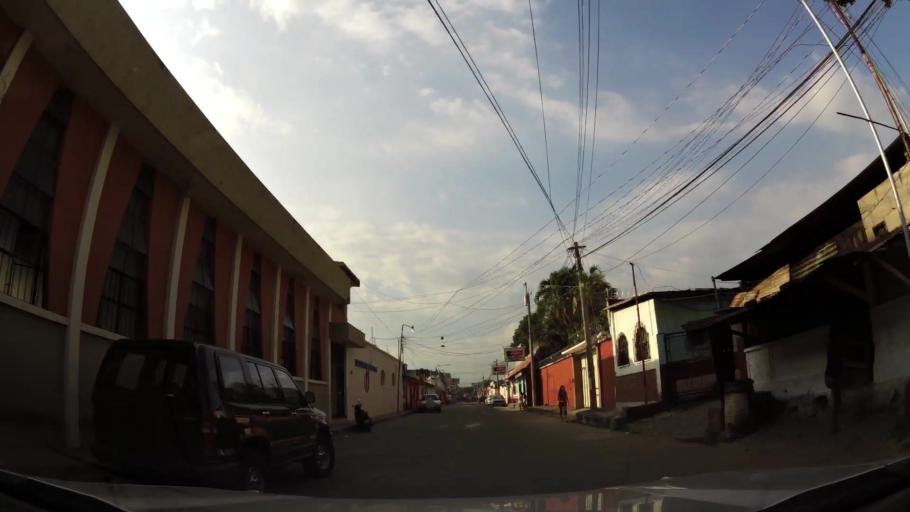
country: GT
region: Retalhuleu
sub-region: Municipio de Retalhuleu
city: Retalhuleu
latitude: 14.5354
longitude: -91.6729
